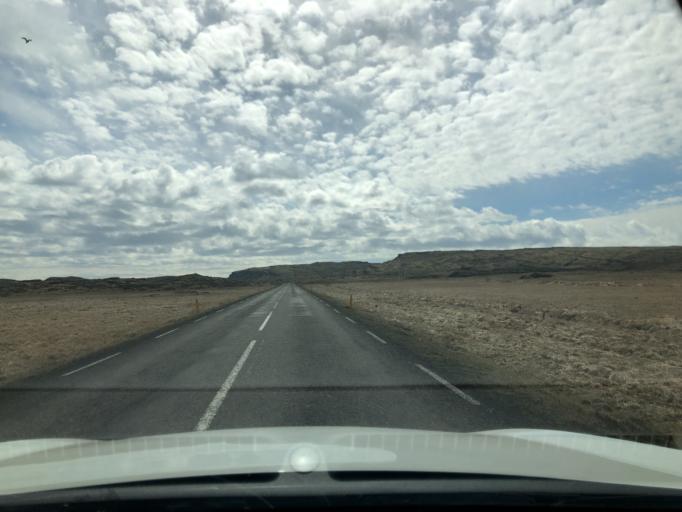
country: IS
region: East
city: Reydarfjoerdur
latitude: 64.6855
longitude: -14.3627
